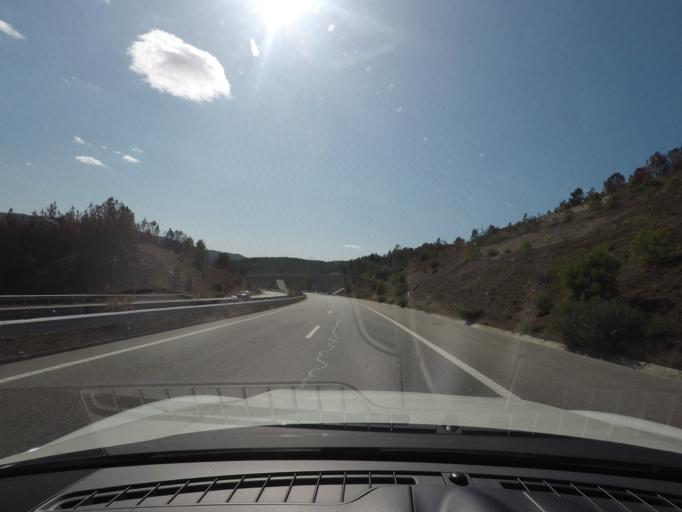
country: PT
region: Vila Real
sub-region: Ribeira de Pena
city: Ribeira de Pena
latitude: 41.4866
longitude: -7.8626
